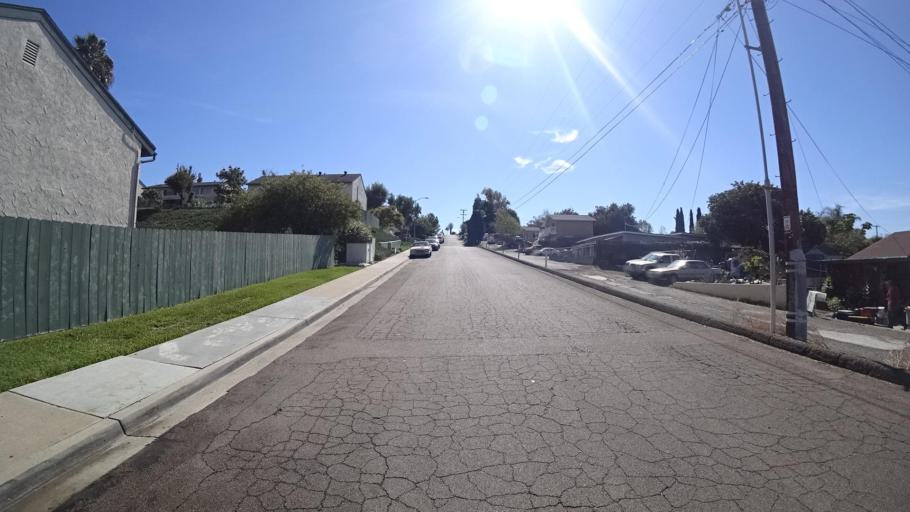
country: US
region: California
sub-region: San Diego County
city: Spring Valley
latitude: 32.7274
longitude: -117.0114
